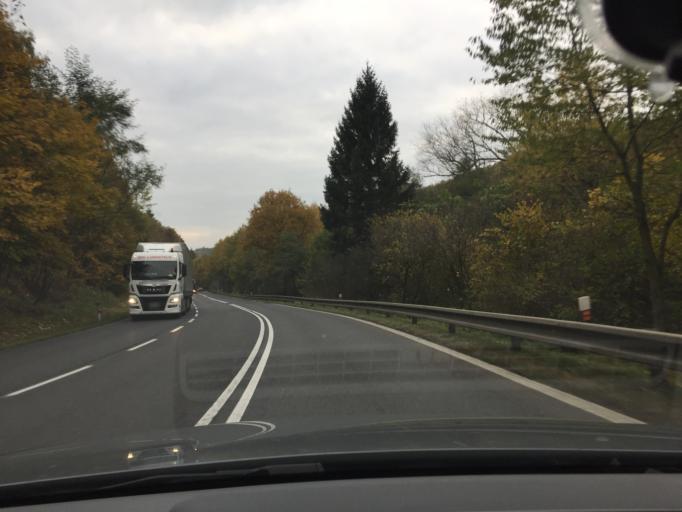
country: CZ
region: Ustecky
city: Rehlovice
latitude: 50.5708
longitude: 13.9545
